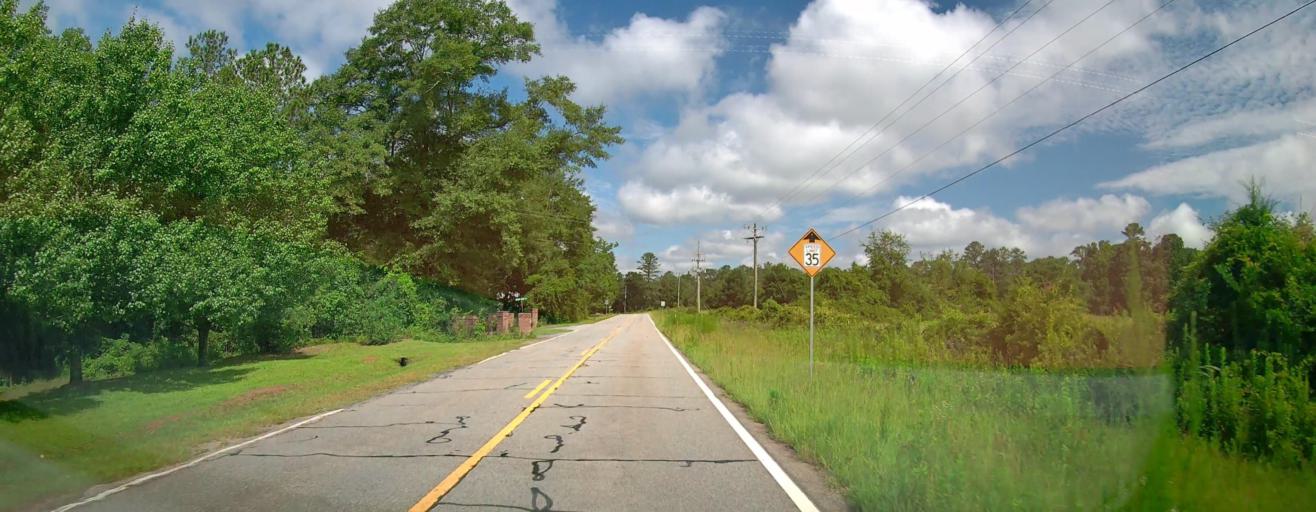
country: US
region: Georgia
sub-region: Peach County
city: Byron
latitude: 32.6005
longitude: -83.7859
